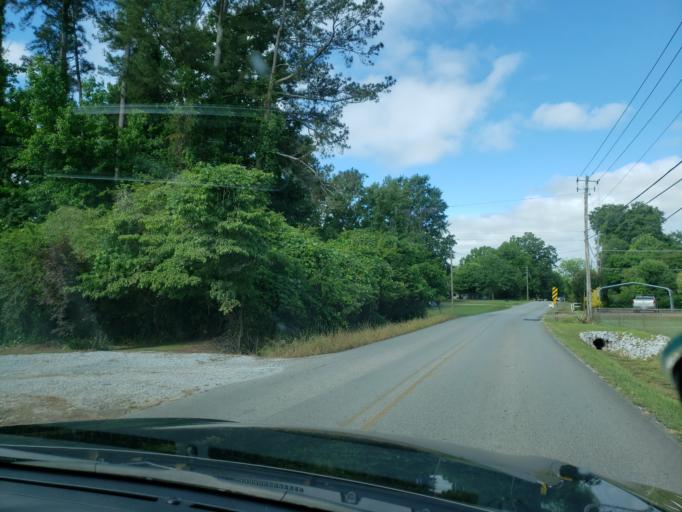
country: US
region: Alabama
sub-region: Calhoun County
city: Weaver
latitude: 33.7520
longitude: -85.8331
